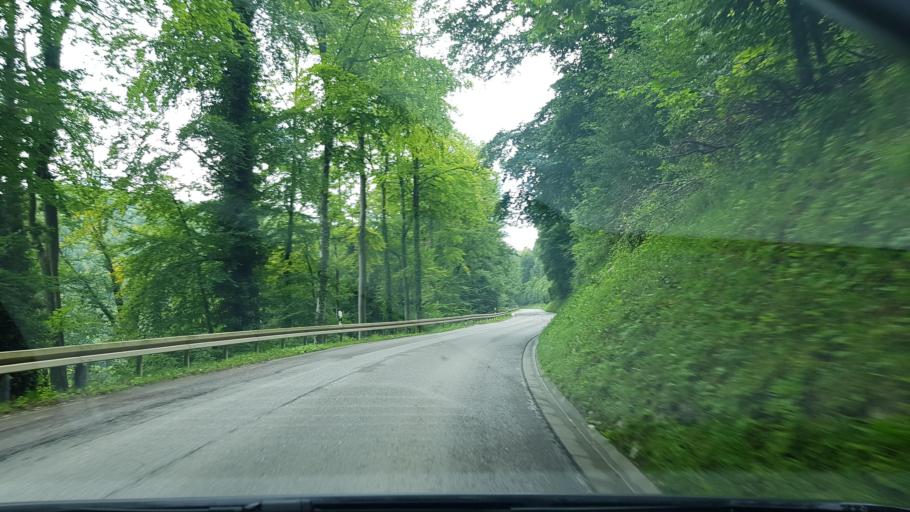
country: DE
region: Baden-Wuerttemberg
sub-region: Tuebingen Region
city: Grabenstetten
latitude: 48.5300
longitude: 9.4934
